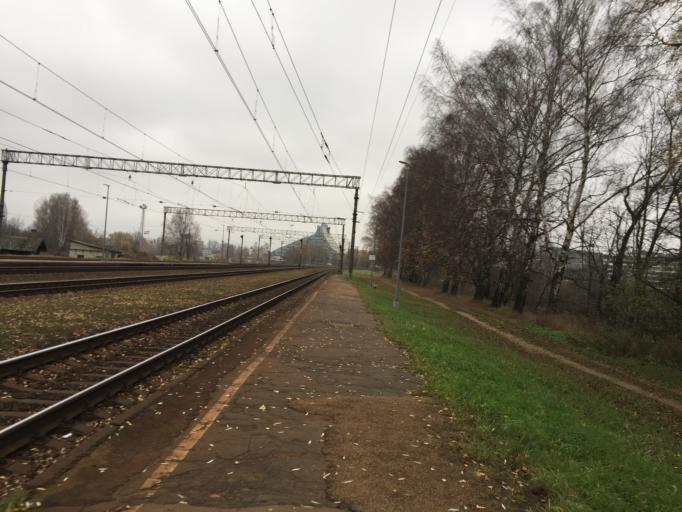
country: LV
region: Riga
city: Riga
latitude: 56.9335
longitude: 24.0902
